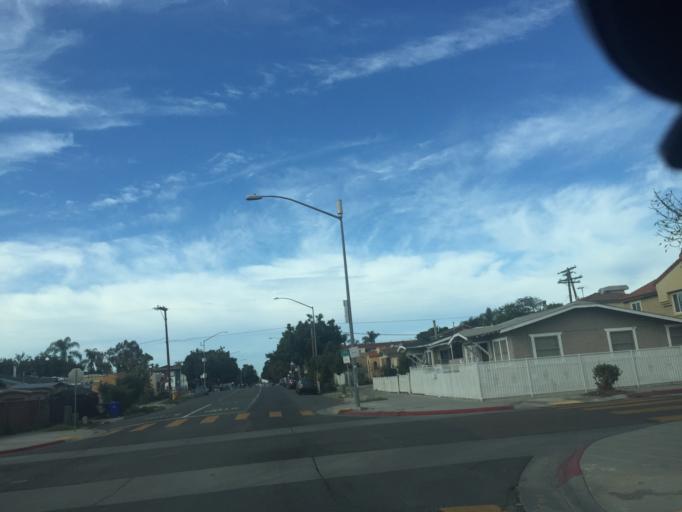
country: US
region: California
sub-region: San Diego County
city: Lemon Grove
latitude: 32.7531
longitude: -117.0942
